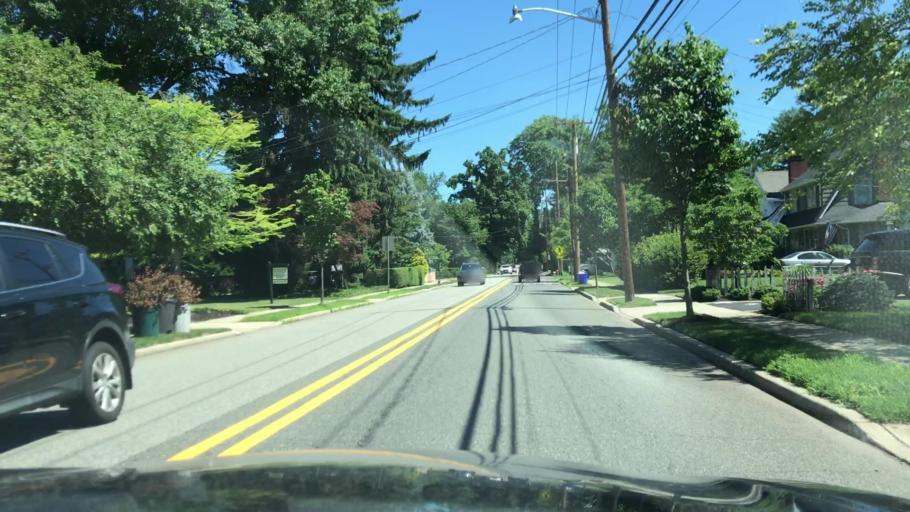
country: US
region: New Jersey
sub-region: Bergen County
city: Ho-Ho-Kus
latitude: 41.0036
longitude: -74.1080
